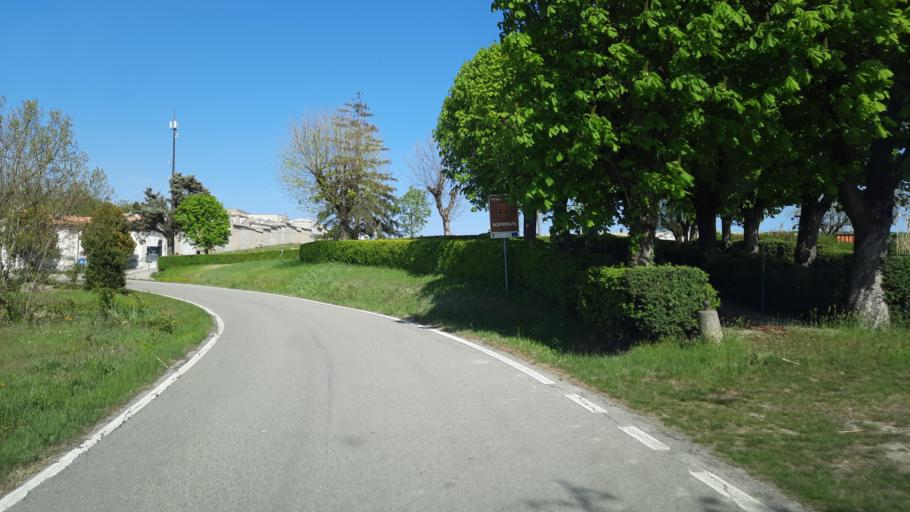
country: IT
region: Piedmont
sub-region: Provincia di Alessandria
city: Camagna Monferrato
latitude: 45.0115
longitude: 8.4272
